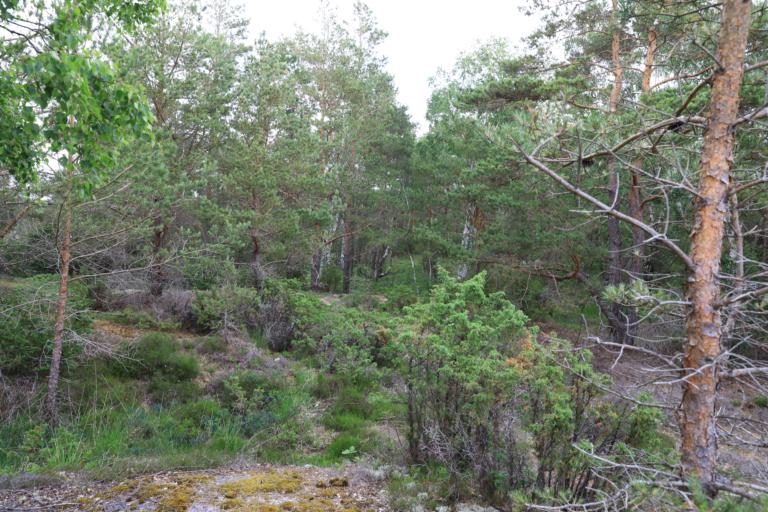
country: SE
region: Halland
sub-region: Varbergs Kommun
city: Varberg
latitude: 57.1725
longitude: 12.2562
